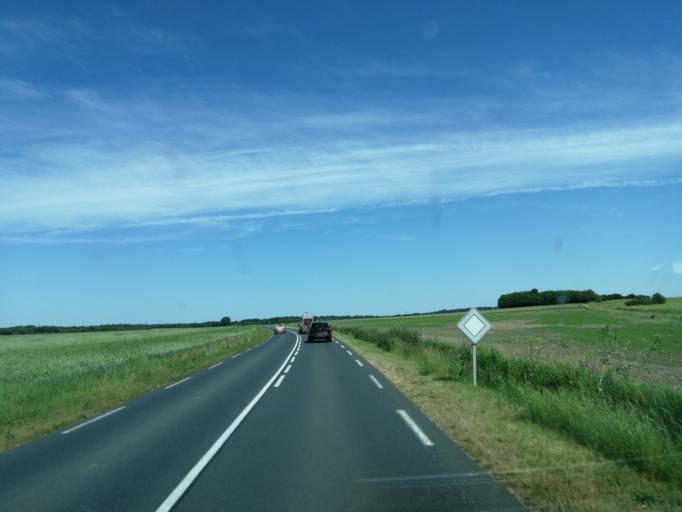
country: FR
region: Poitou-Charentes
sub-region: Departement des Deux-Sevres
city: Saint-Leger-de-Montbrun
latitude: 46.9697
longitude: -0.1393
